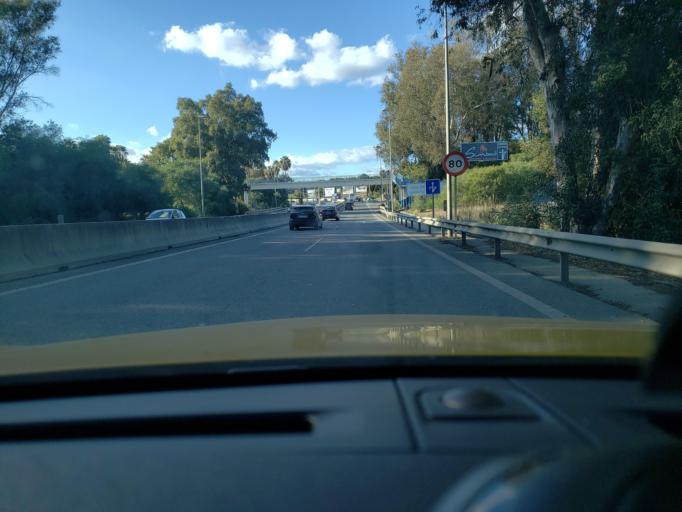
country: ES
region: Andalusia
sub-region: Provincia de Malaga
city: Ojen
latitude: 36.4917
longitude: -4.7493
